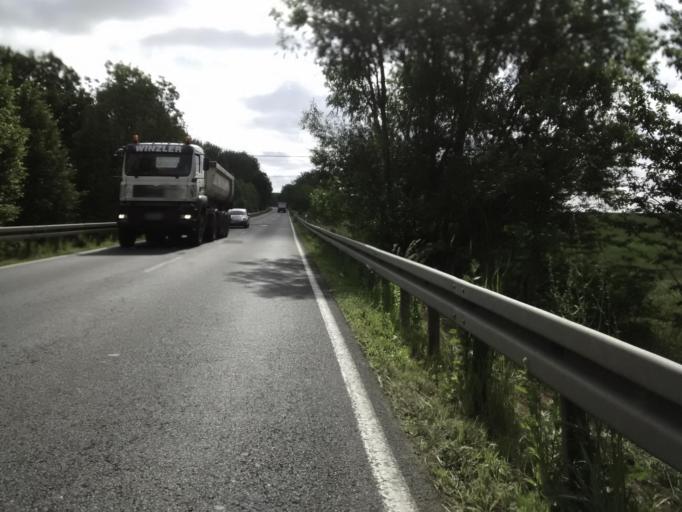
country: DE
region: Berlin
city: Blankenfelde
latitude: 52.6640
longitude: 13.3952
